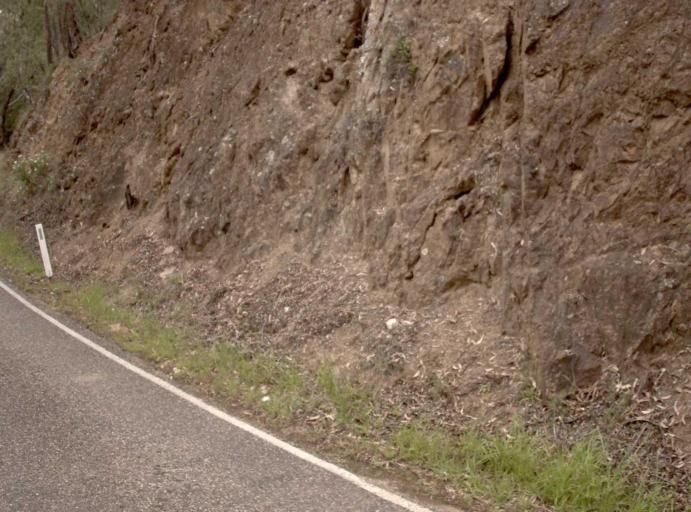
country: AU
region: Victoria
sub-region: East Gippsland
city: Bairnsdale
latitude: -37.5417
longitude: 147.2051
